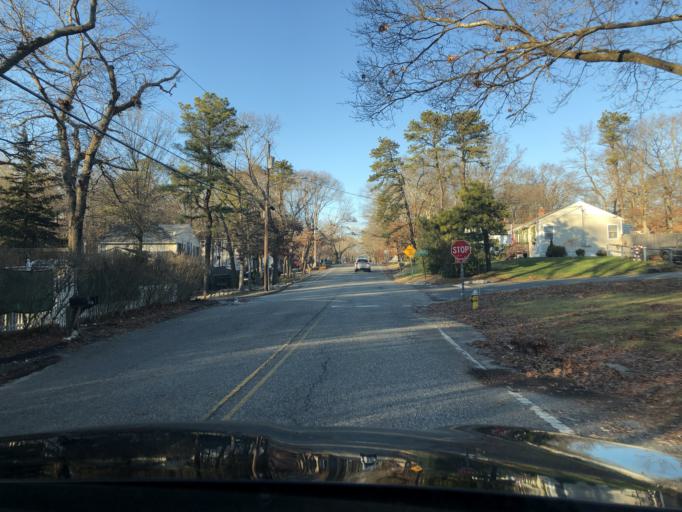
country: US
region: New York
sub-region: Suffolk County
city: Wading River
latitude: 40.9155
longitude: -72.8474
